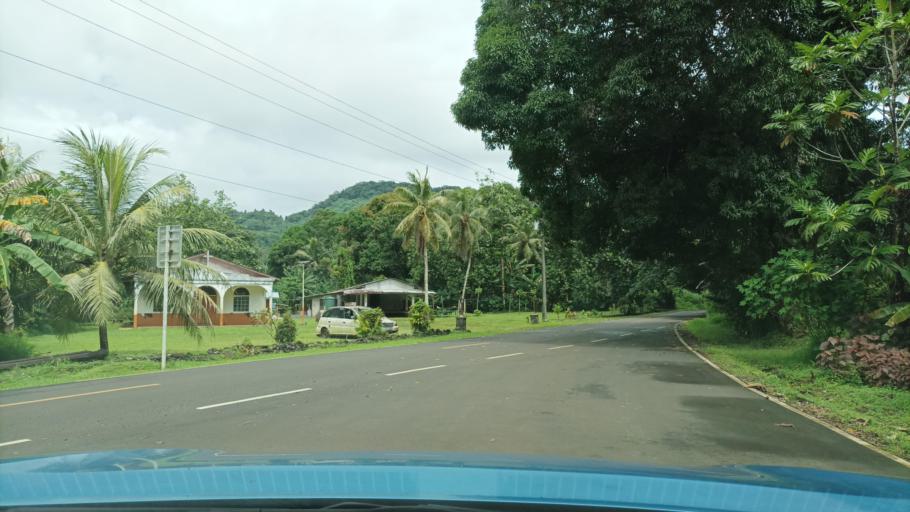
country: FM
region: Pohnpei
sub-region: Madolenihm Municipality
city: Madolenihm Municipality Government
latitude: 6.8896
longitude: 158.3142
